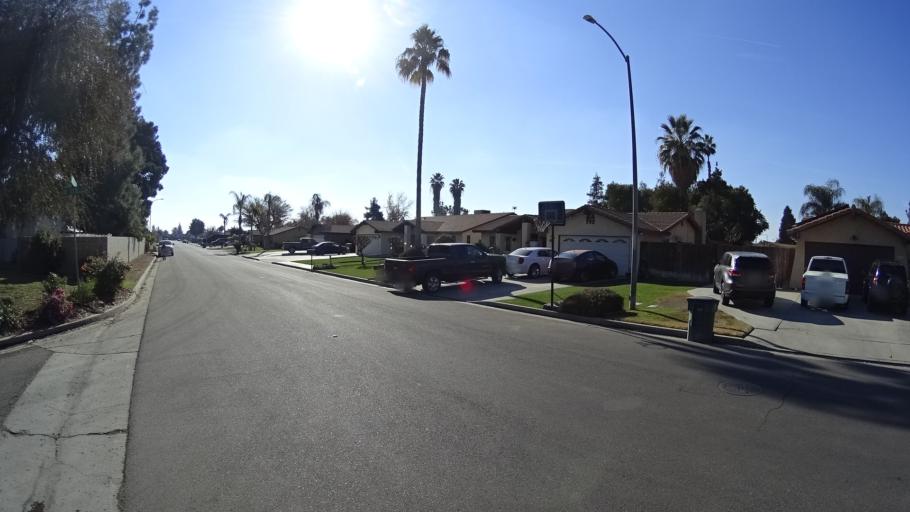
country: US
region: California
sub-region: Kern County
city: Greenfield
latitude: 35.3060
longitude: -119.0412
